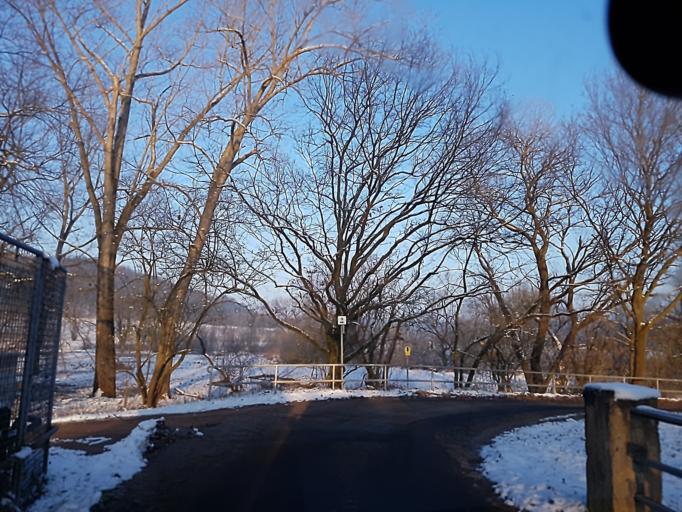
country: DE
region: Saxony
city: Grossweitzschen
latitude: 51.1471
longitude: 13.0111
